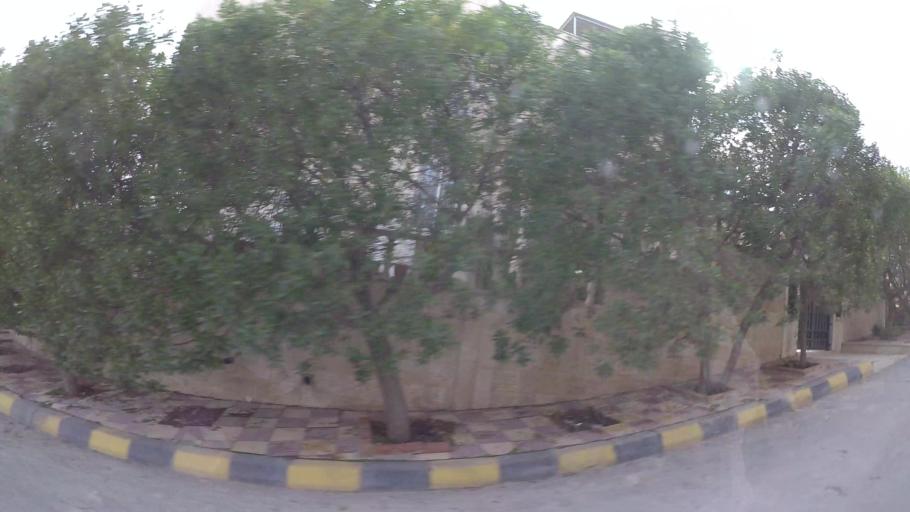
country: JO
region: Amman
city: Amman
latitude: 32.0129
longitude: 35.9448
